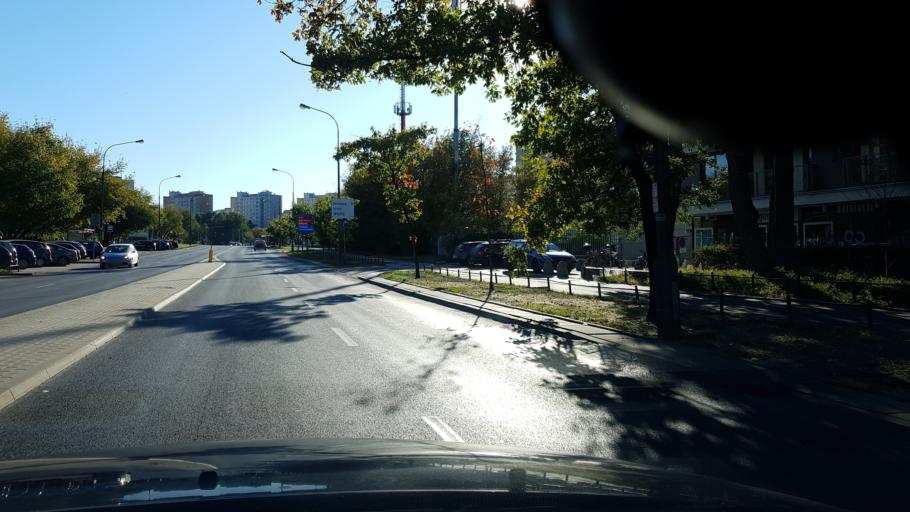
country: PL
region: Masovian Voivodeship
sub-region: Warszawa
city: Bielany
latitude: 52.2828
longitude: 20.9261
